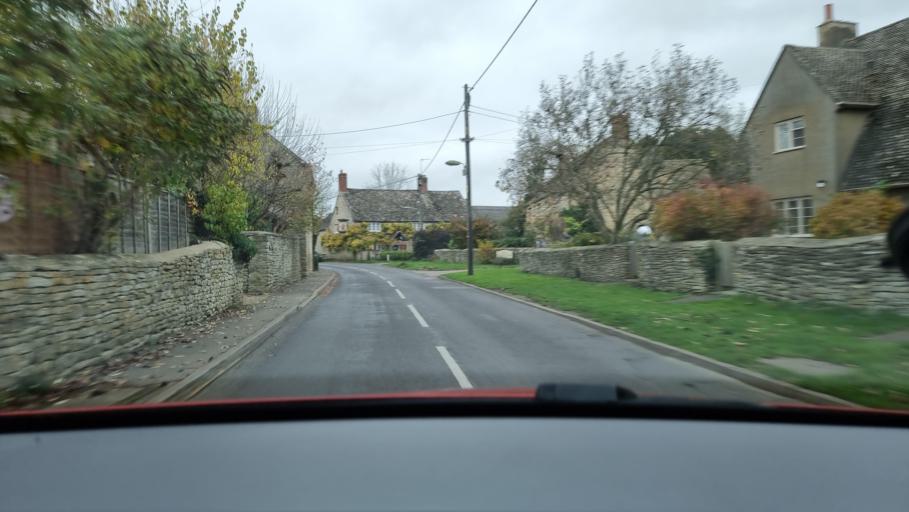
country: GB
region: England
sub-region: Oxfordshire
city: Woodstock
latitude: 51.8806
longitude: -1.3068
